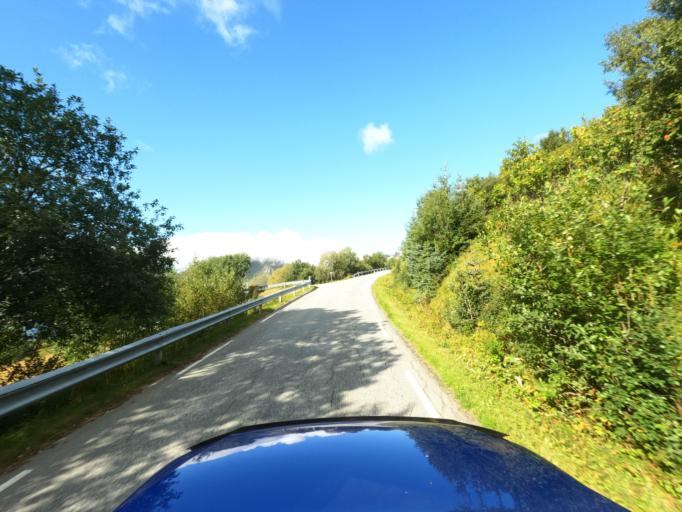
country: NO
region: Nordland
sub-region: Vagan
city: Kabelvag
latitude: 68.2893
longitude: 14.3279
